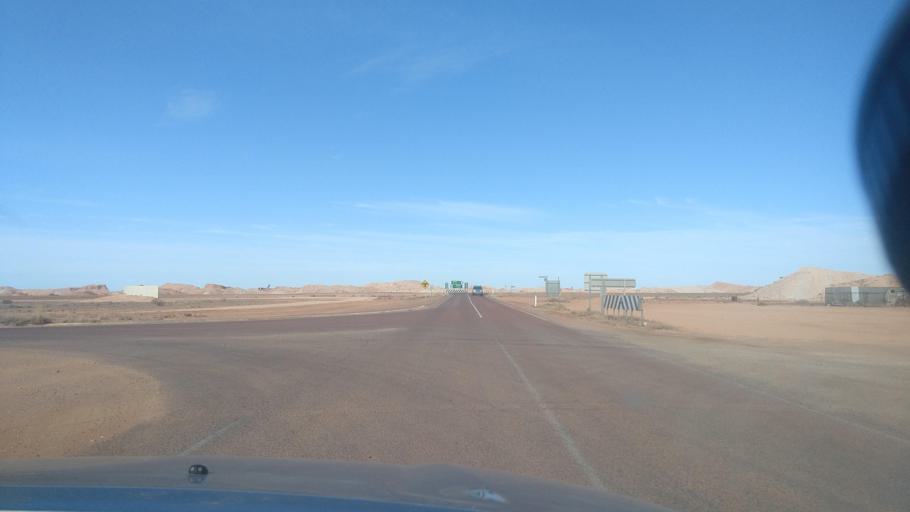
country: AU
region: South Australia
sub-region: Coober Pedy
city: Coober Pedy
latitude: -29.0213
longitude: 134.7444
